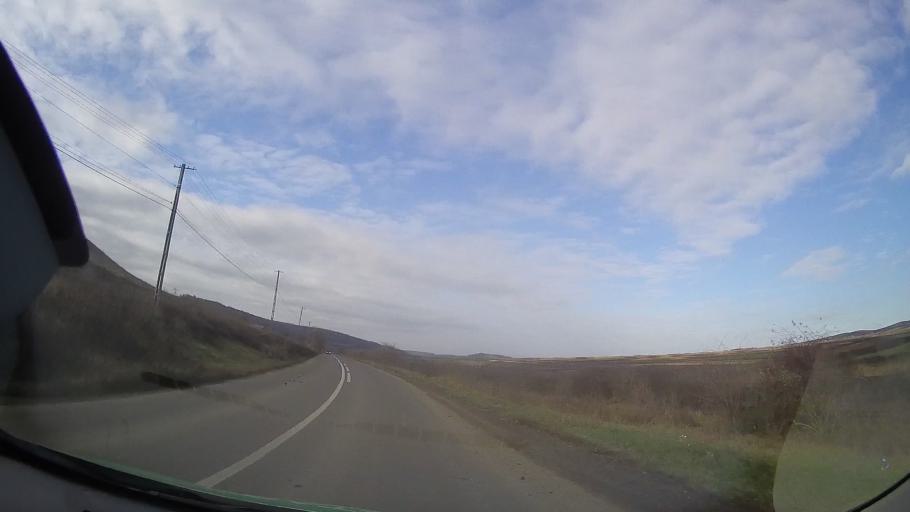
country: RO
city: Barza
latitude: 46.5489
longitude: 24.1211
